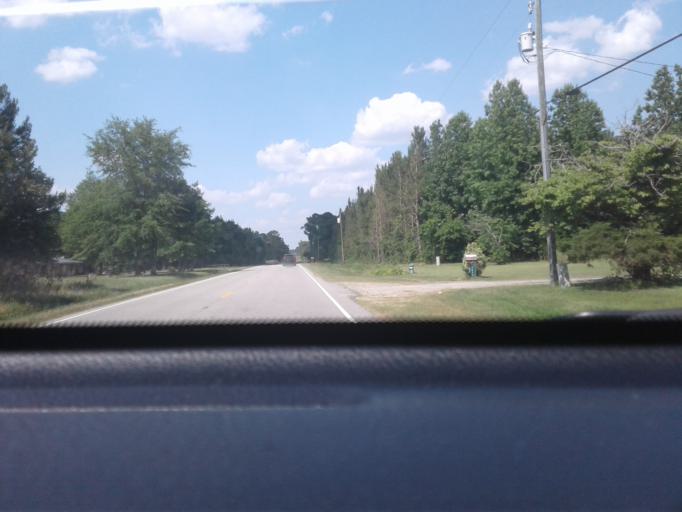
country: US
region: North Carolina
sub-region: Harnett County
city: Erwin
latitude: 35.1967
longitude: -78.6929
